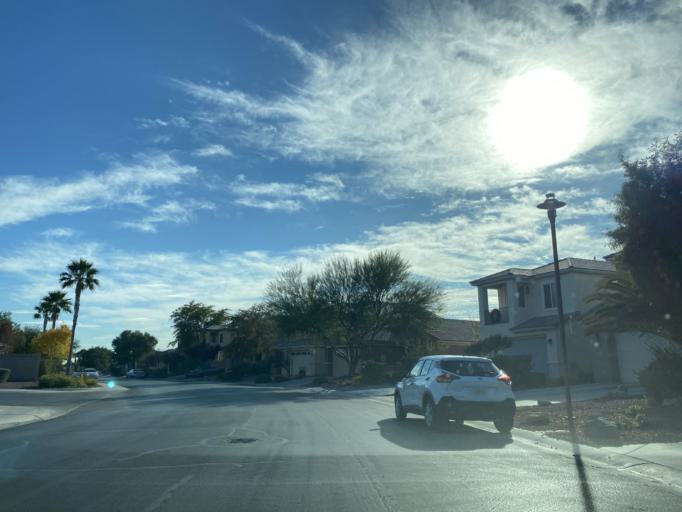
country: US
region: Nevada
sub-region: Clark County
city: North Las Vegas
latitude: 36.3157
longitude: -115.2438
